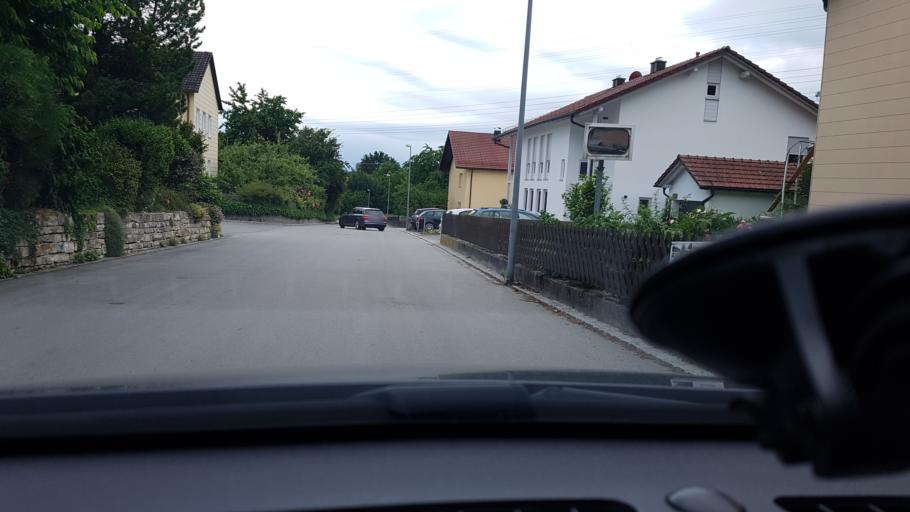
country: AT
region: Upper Austria
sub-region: Politischer Bezirk Braunau am Inn
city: Braunau am Inn
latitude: 48.2760
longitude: 13.0439
